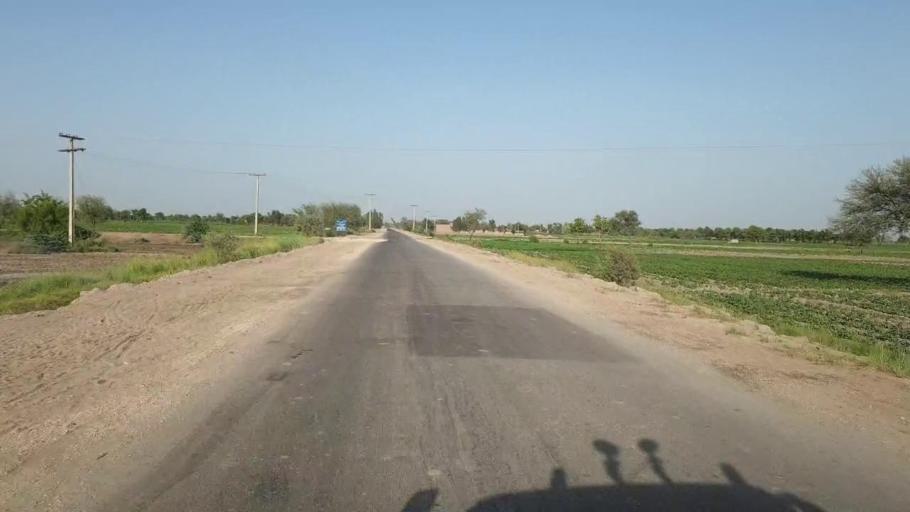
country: PK
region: Sindh
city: Jam Sahib
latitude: 26.3489
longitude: 68.5475
